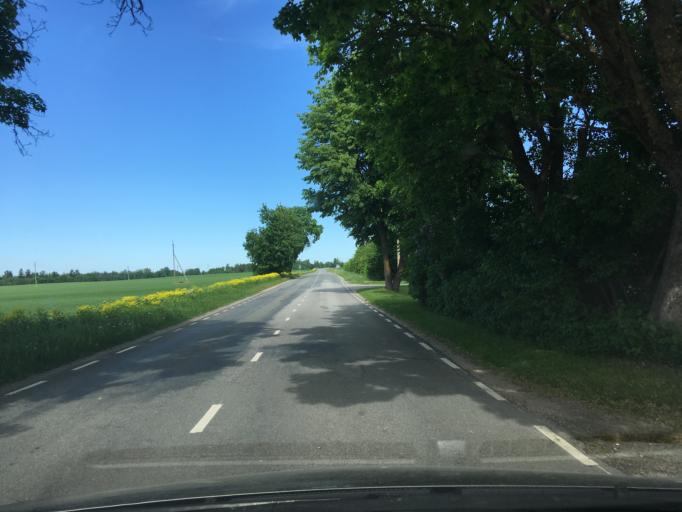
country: EE
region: Harju
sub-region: Raasiku vald
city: Raasiku
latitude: 59.1075
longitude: 25.1673
